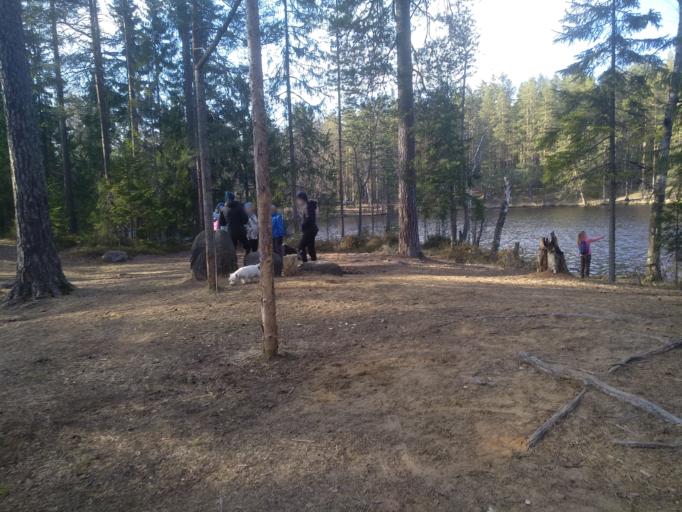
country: RU
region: Leningrad
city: Sosnovo
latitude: 60.5885
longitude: 30.0992
